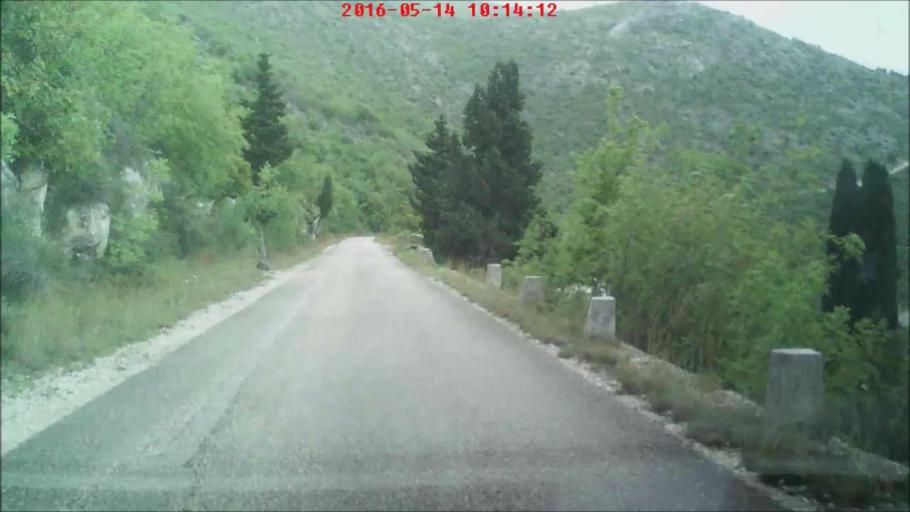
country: HR
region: Dubrovacko-Neretvanska
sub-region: Grad Dubrovnik
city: Mokosica
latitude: 42.7340
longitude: 17.9573
